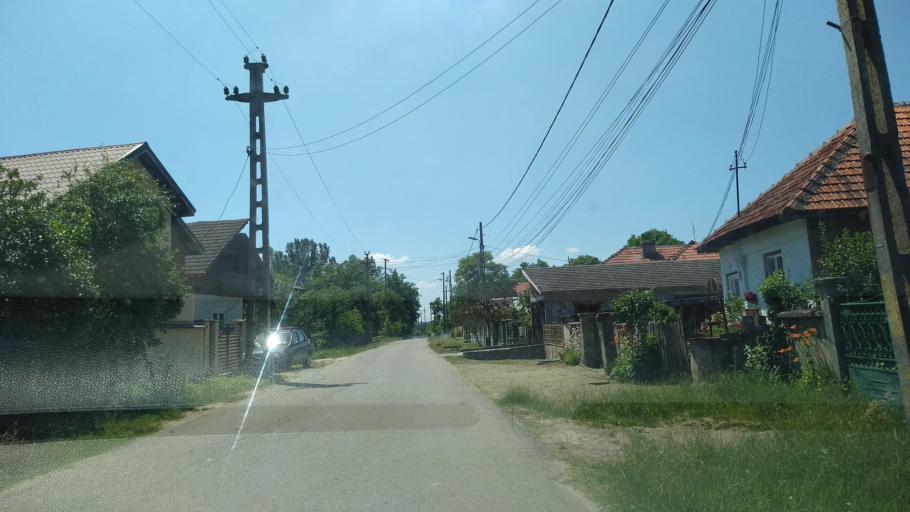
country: RO
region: Gorj
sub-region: Comuna Turcinesti
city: Turcinesti
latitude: 45.1134
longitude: 23.3162
